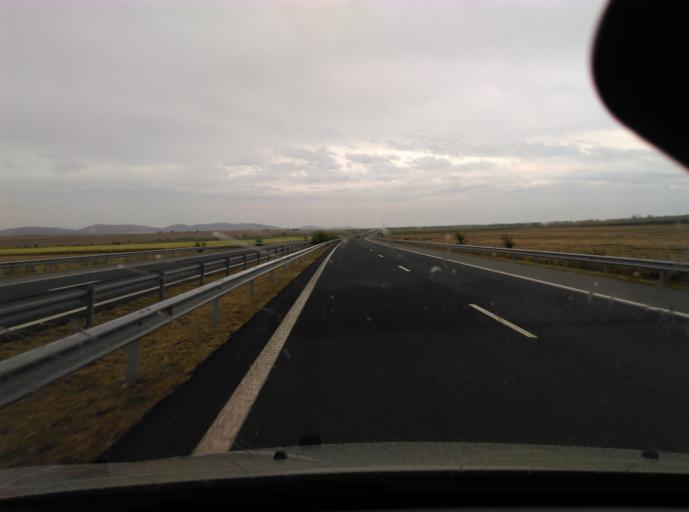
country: BG
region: Sliven
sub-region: Obshtina Nova Zagora
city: Nova Zagora
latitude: 42.4733
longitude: 26.1054
